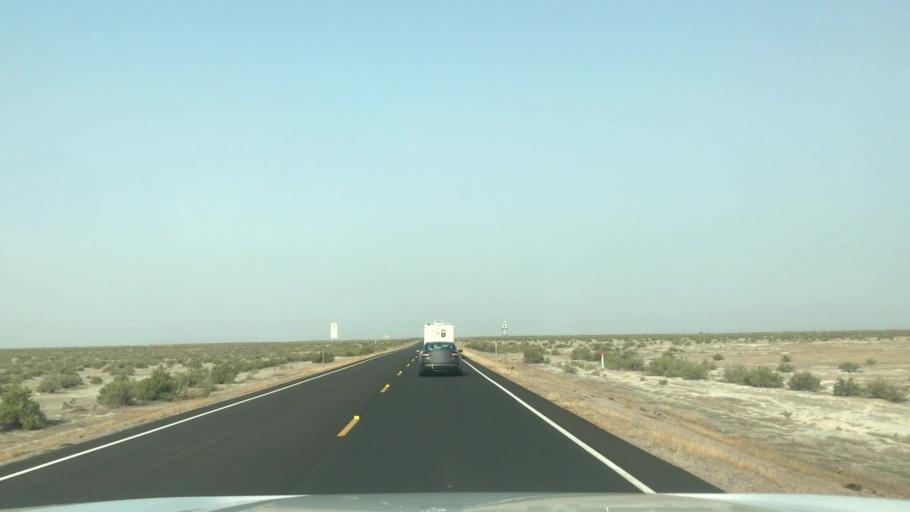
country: US
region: Utah
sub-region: Millard County
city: Delta
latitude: 39.3135
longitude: -112.7567
